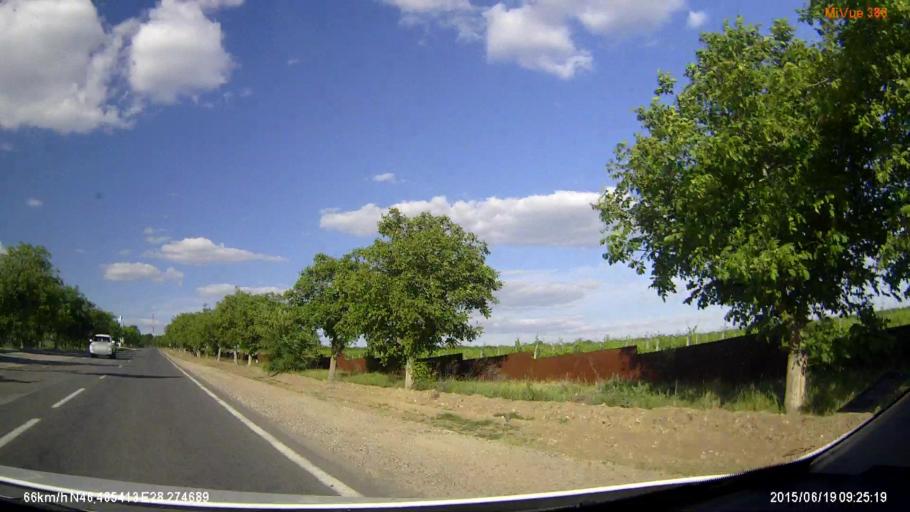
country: MD
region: Leova
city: Leova
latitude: 46.4853
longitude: 28.2745
